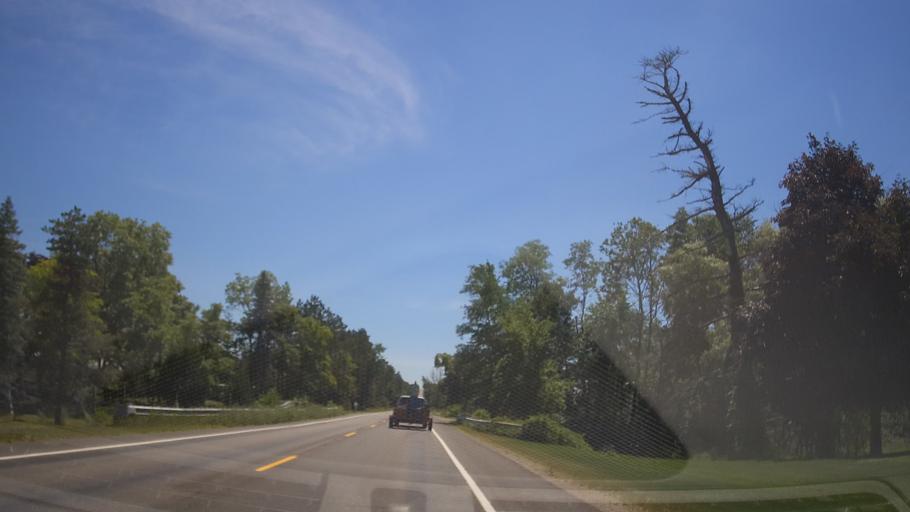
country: US
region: Michigan
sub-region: Grand Traverse County
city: Traverse City
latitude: 44.6400
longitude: -85.6964
